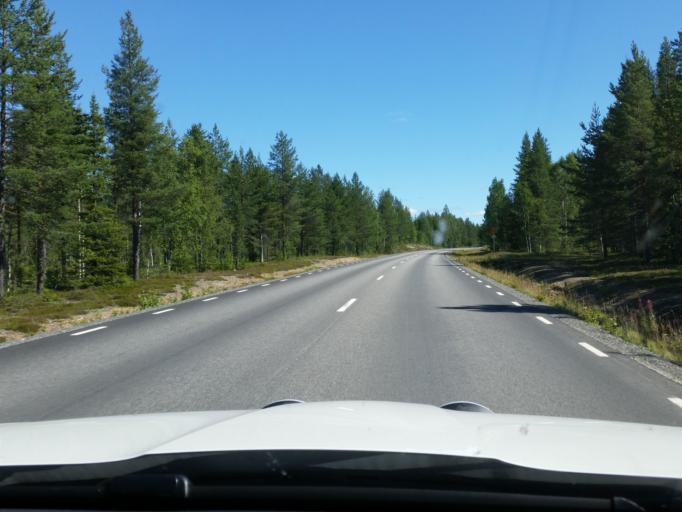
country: SE
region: Vaesterbotten
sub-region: Skelleftea Kommun
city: Storvik
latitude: 65.3351
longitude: 20.8608
